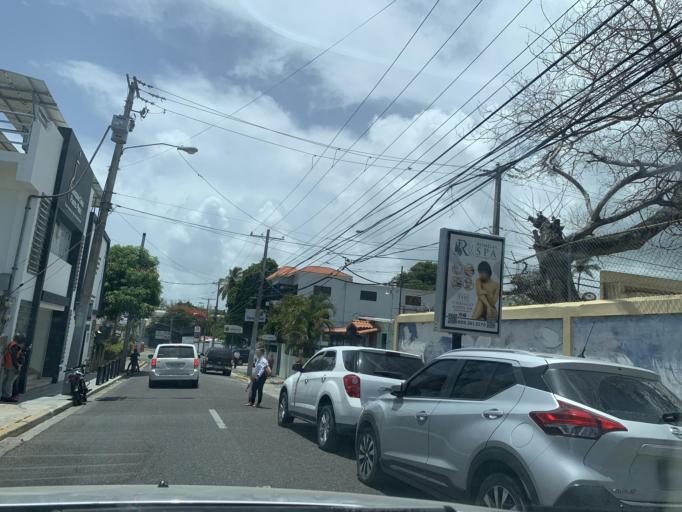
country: DO
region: Puerto Plata
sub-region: Puerto Plata
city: Puerto Plata
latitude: 19.7950
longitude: -70.6876
